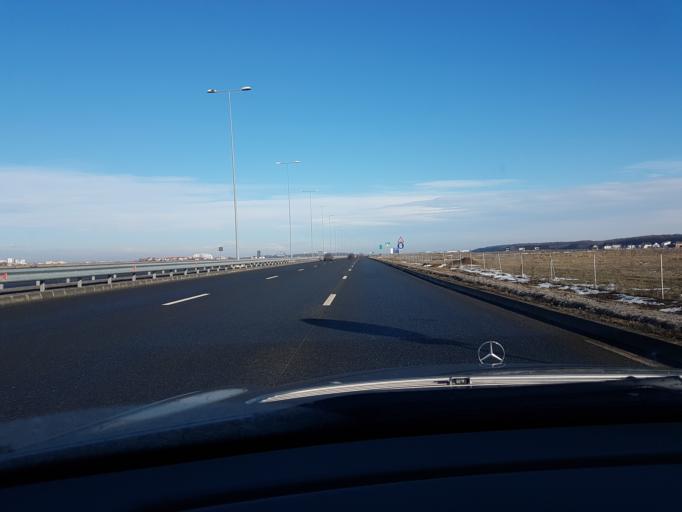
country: RO
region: Ilfov
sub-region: Voluntari City
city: Voluntari
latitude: 44.4977
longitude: 26.1527
